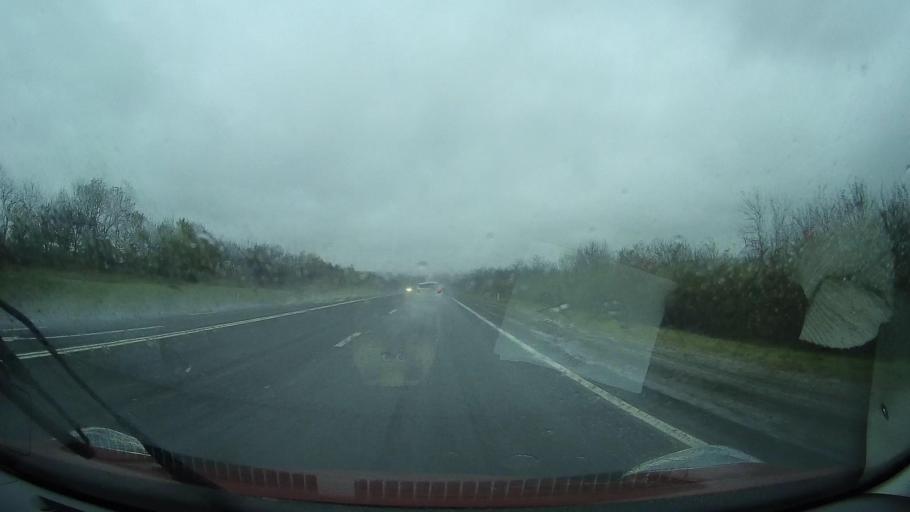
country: RU
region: Stavropol'skiy
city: Nevinnomyssk
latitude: 44.6217
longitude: 42.0818
